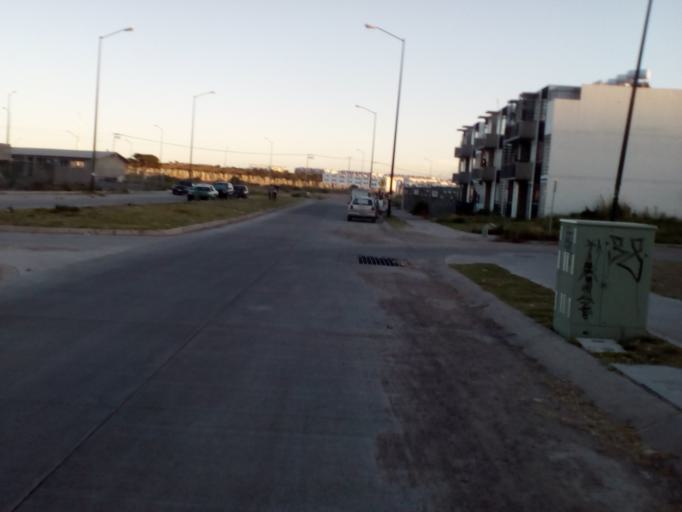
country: MX
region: Guanajuato
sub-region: Leon
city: Fraccionamiento Paseo de las Torres
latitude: 21.1833
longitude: -101.7668
